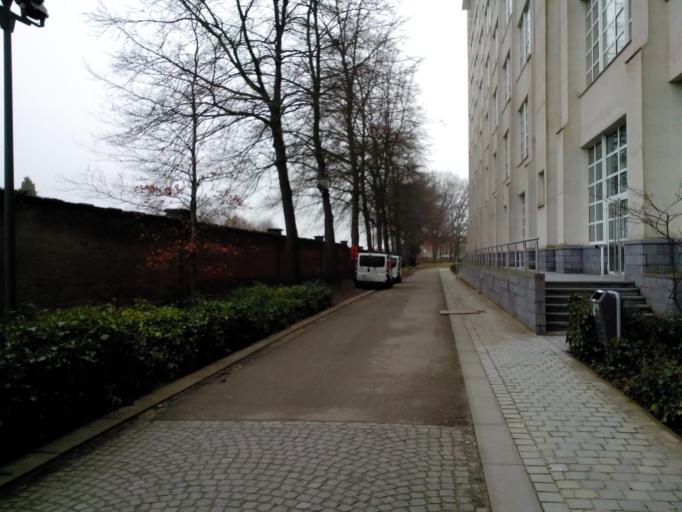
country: BE
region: Flanders
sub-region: Provincie Vlaams-Brabant
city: Leuven
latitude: 50.8680
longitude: 4.7129
